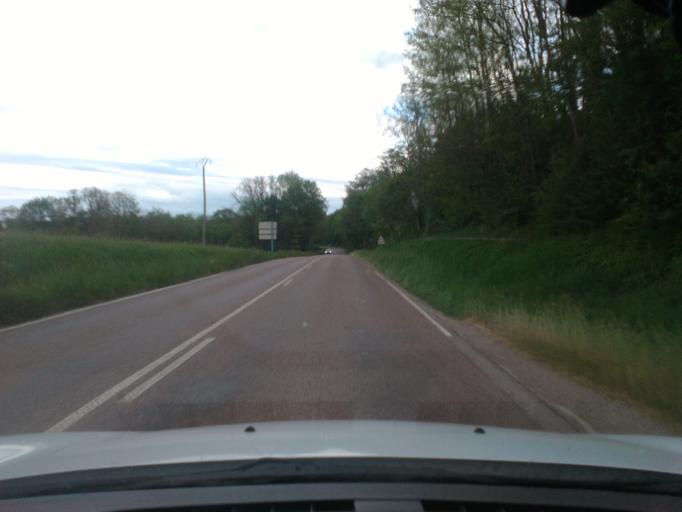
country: FR
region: Lorraine
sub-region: Departement des Vosges
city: Mirecourt
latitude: 48.3069
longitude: 6.0694
